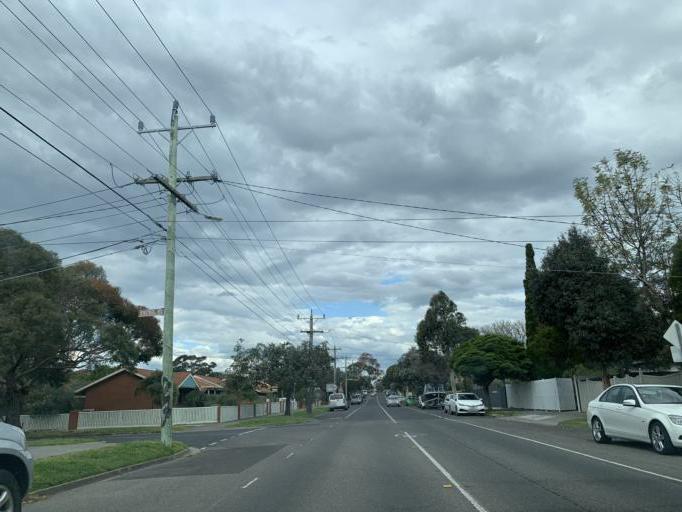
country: AU
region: Victoria
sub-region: Bayside
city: Hampton
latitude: -37.9332
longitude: 145.0052
